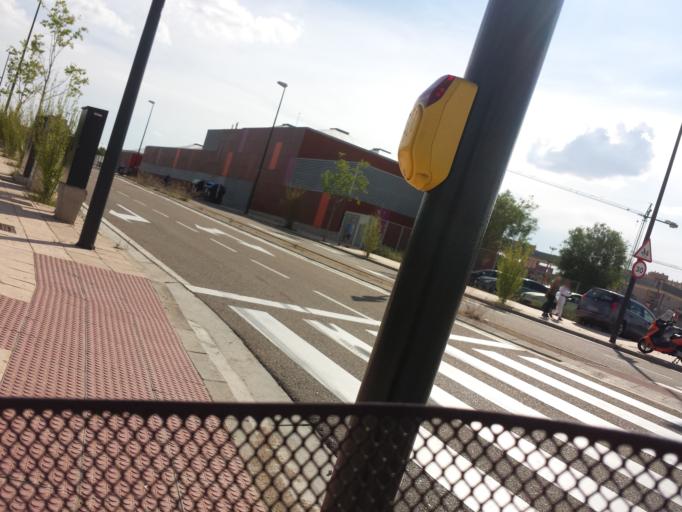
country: ES
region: Aragon
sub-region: Provincia de Zaragoza
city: Montecanal
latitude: 41.6354
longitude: -0.9391
